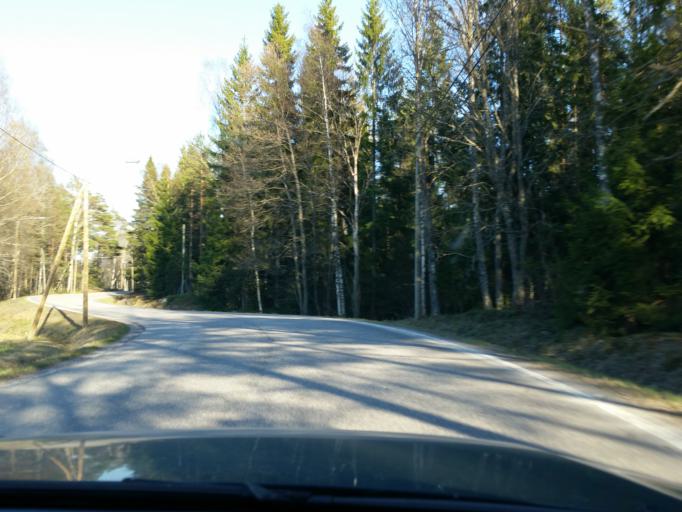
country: FI
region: Uusimaa
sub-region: Helsinki
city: Kirkkonummi
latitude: 60.1125
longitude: 24.5576
